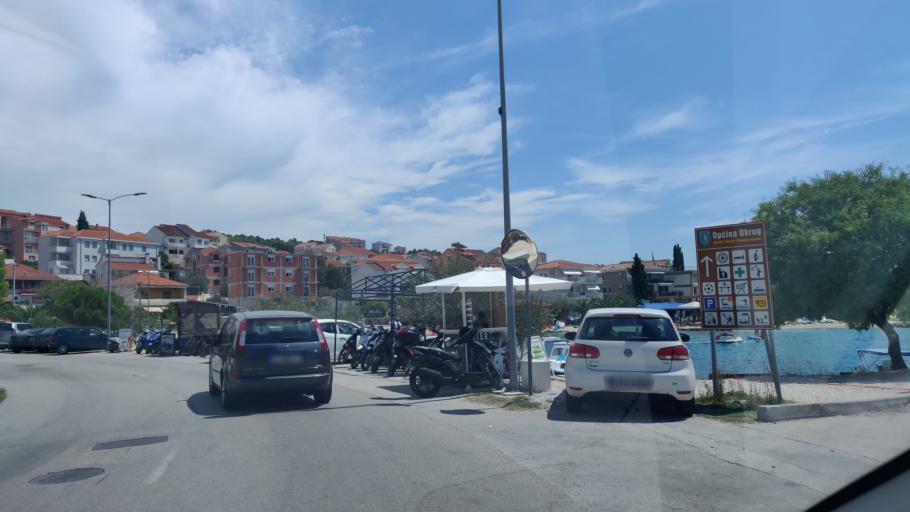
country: HR
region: Splitsko-Dalmatinska
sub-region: Grad Trogir
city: Trogir
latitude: 43.5028
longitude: 16.2584
